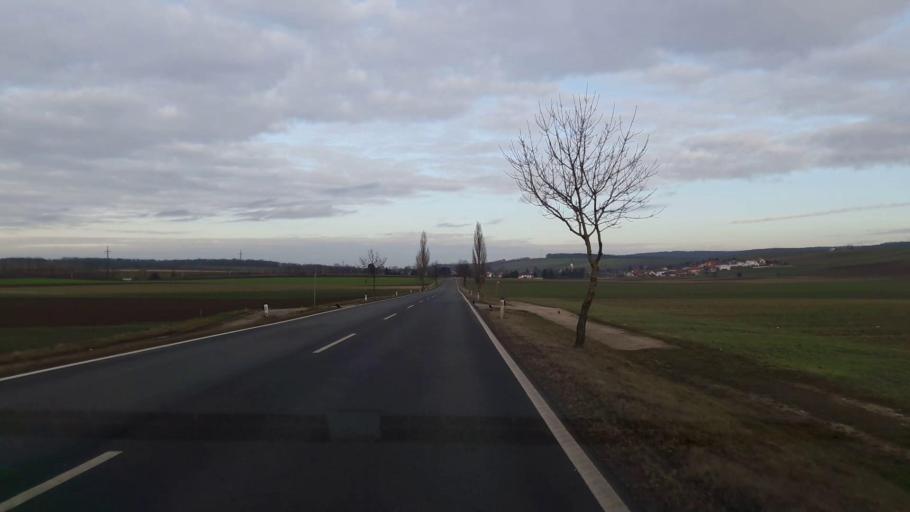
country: AT
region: Lower Austria
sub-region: Politischer Bezirk Mistelbach
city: Mistelbach
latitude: 48.5949
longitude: 16.5464
